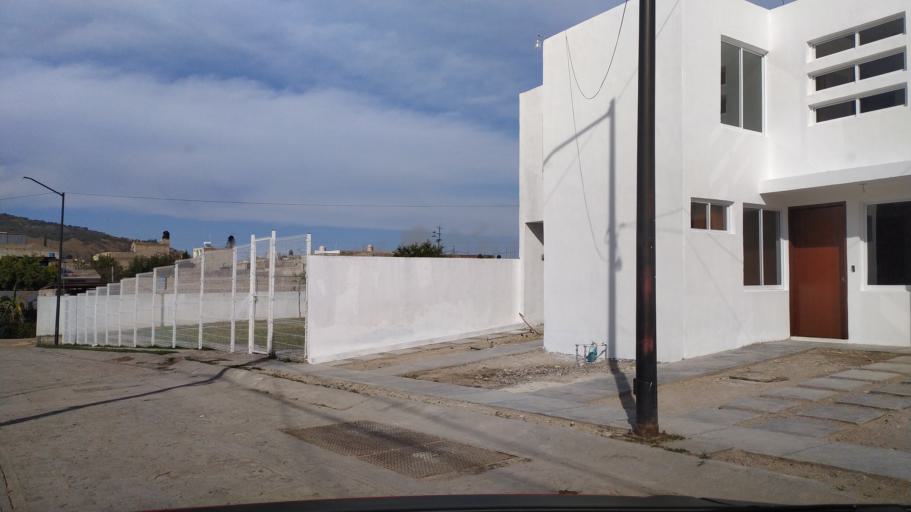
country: MX
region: Jalisco
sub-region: Tlajomulco de Zuniga
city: Palomar
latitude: 20.6317
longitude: -103.4714
